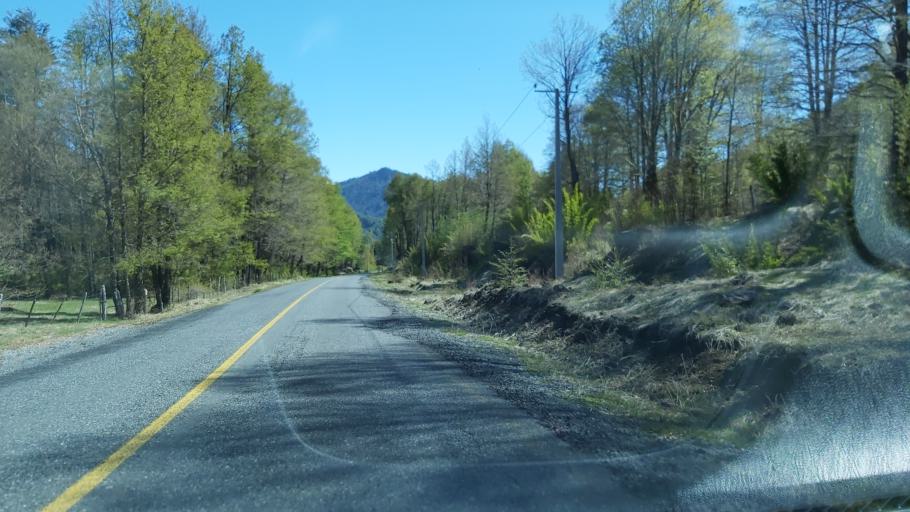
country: CL
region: Araucania
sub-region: Provincia de Cautin
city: Vilcun
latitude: -38.4657
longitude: -71.5193
